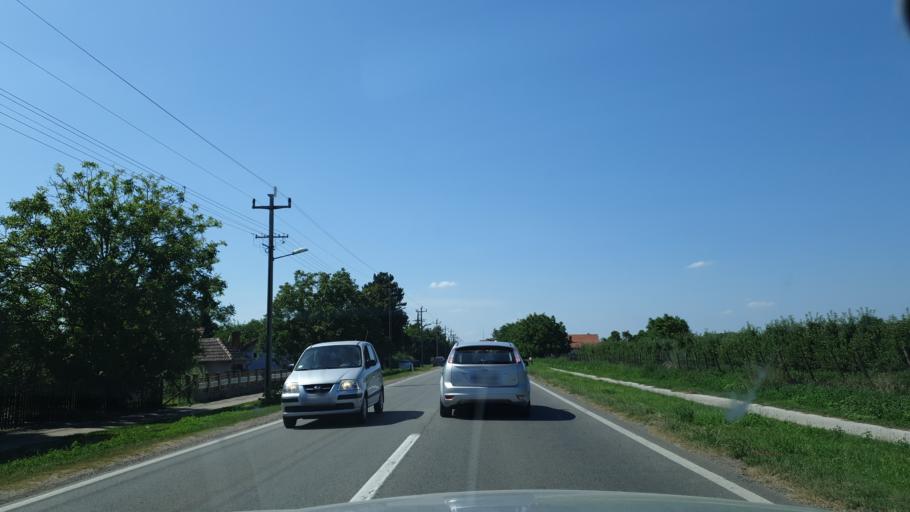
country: HU
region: Bacs-Kiskun
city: Kelebia
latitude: 46.1409
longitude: 19.5902
